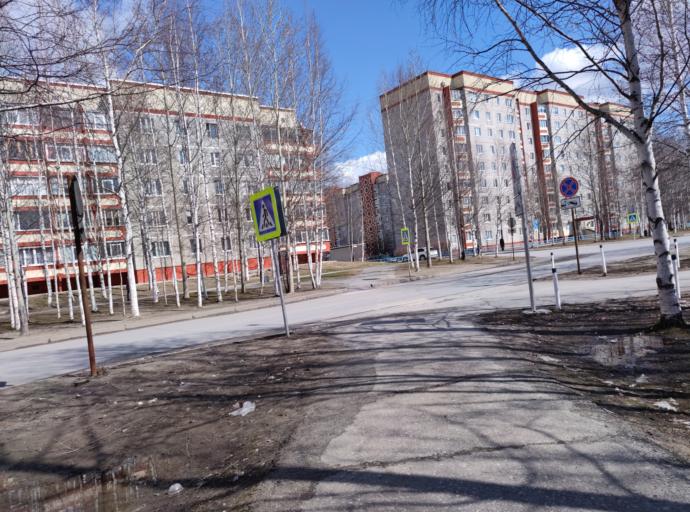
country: RU
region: Khanty-Mansiyskiy Avtonomnyy Okrug
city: Langepas
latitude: 61.2508
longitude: 75.1782
